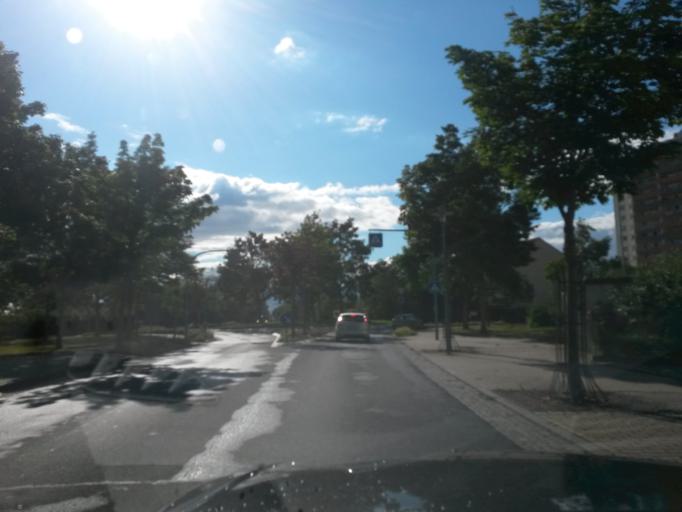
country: DE
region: Bavaria
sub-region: Regierungsbezirk Unterfranken
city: Rottendorf
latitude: 49.7909
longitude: 10.0202
